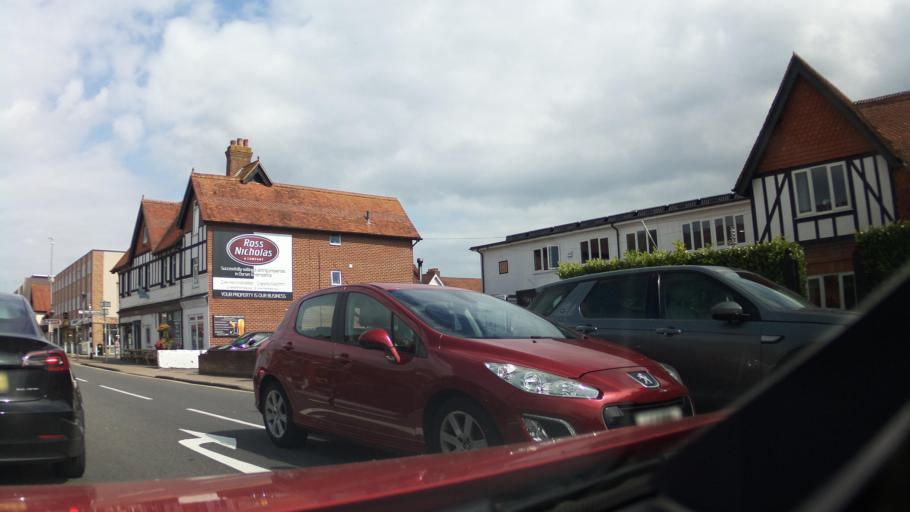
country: GB
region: England
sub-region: Hampshire
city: New Milton
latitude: 50.7420
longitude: -1.6975
